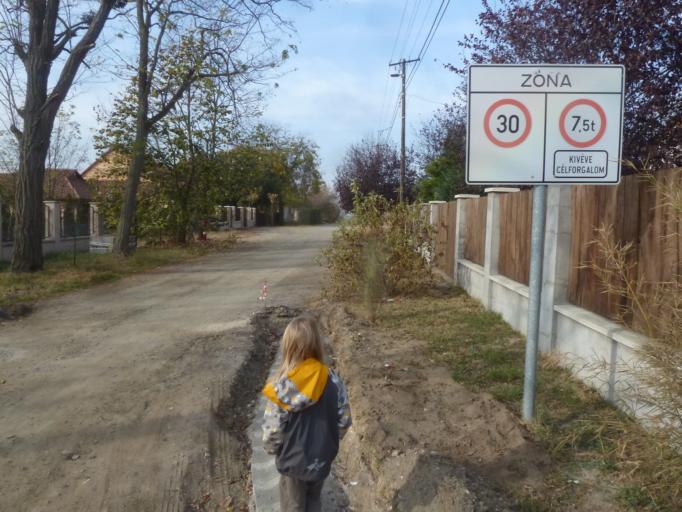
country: HU
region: Pest
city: Szada
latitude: 47.6251
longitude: 19.3160
